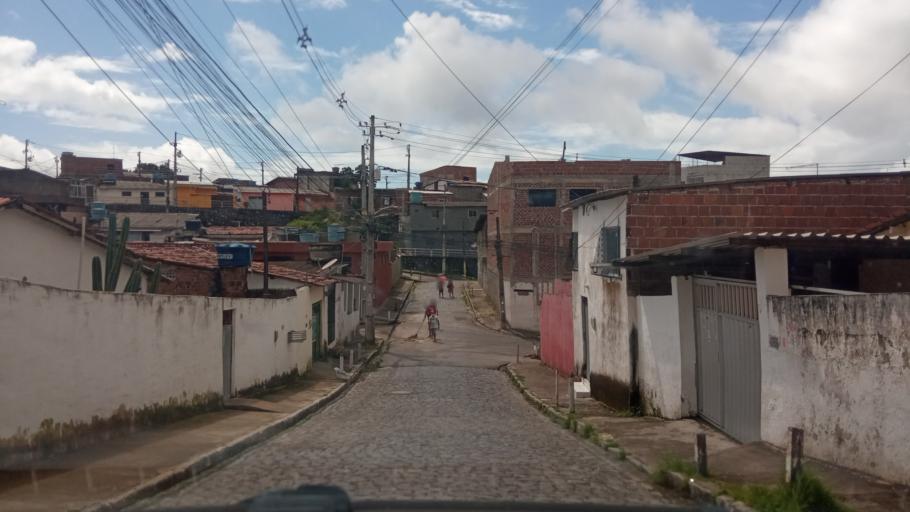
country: BR
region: Pernambuco
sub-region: Jaboatao Dos Guararapes
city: Jaboatao dos Guararapes
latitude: -8.1332
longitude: -34.9532
